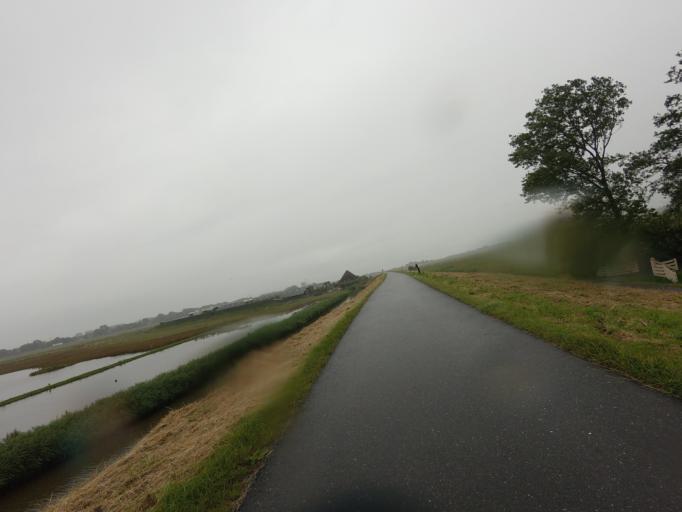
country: NL
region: North Holland
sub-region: Gemeente Schagen
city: Schagen
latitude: 52.8065
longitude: 4.7899
